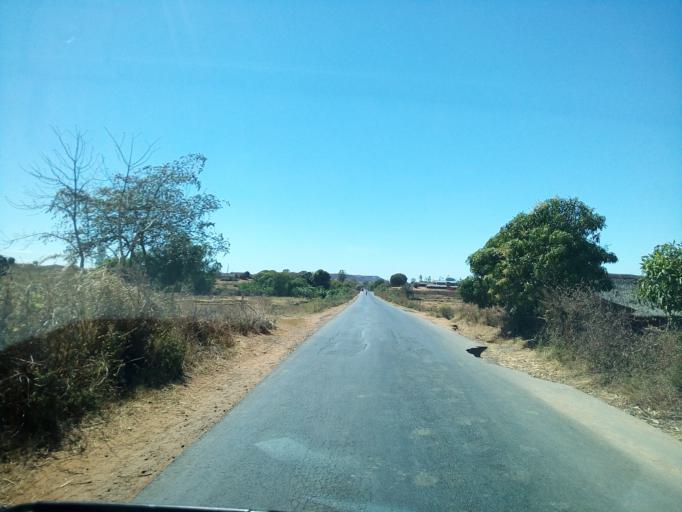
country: MG
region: Boeny
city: Ambato Boeny
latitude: -16.3799
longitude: 46.9510
